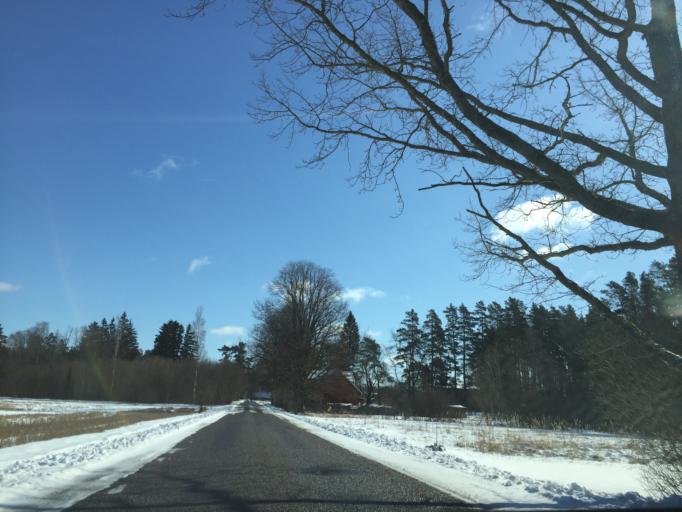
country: LV
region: Aloja
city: Staicele
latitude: 57.9970
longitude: 24.5792
